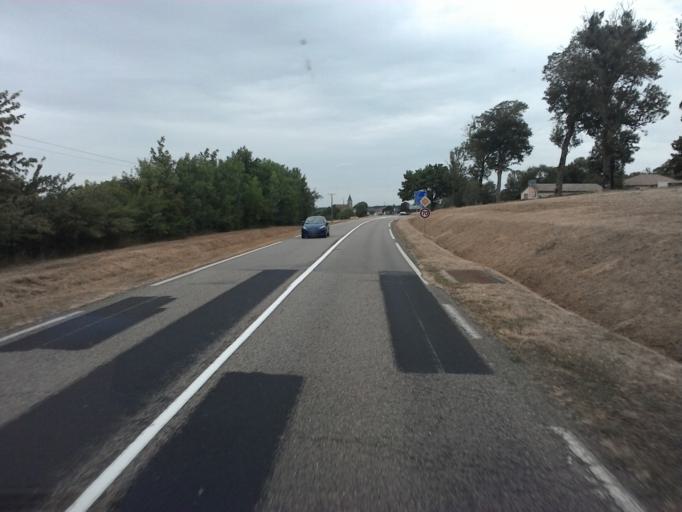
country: FR
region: Lorraine
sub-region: Departement de Meurthe-et-Moselle
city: Colombey-les-Belles
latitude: 48.5424
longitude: 5.9052
